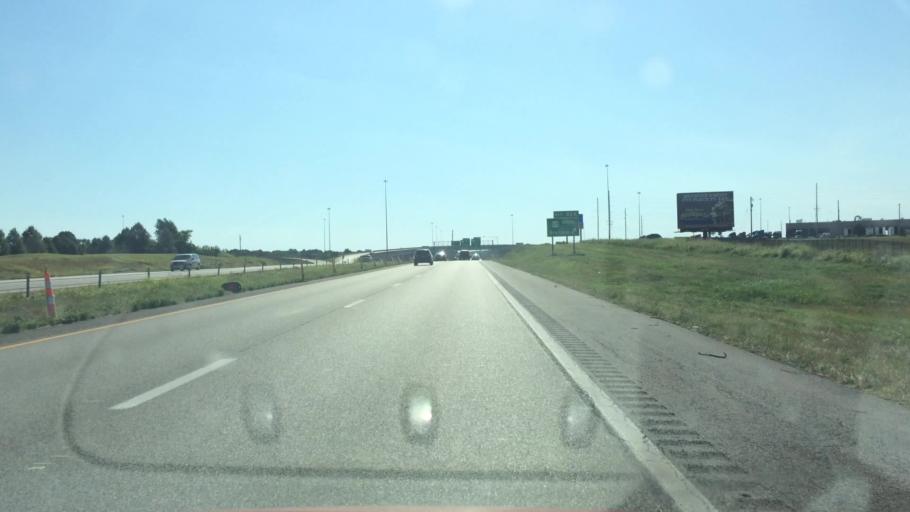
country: US
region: Missouri
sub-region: Greene County
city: Springfield
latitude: 37.2501
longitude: -93.2324
